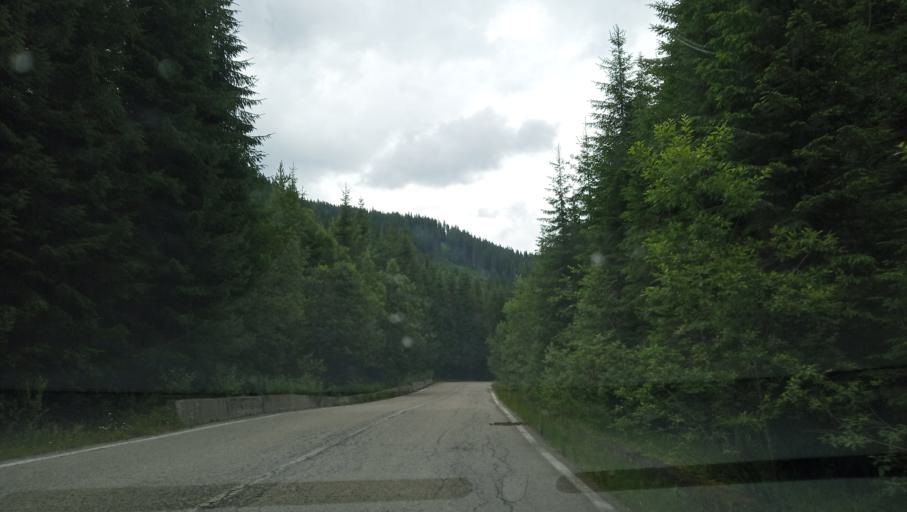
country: RO
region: Valcea
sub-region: Comuna Voineasa
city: Voineasa
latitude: 45.4232
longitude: 23.7640
